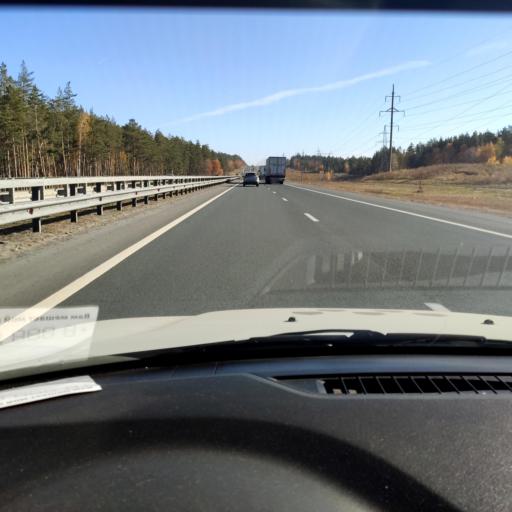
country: RU
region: Samara
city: Povolzhskiy
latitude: 53.5174
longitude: 49.7595
